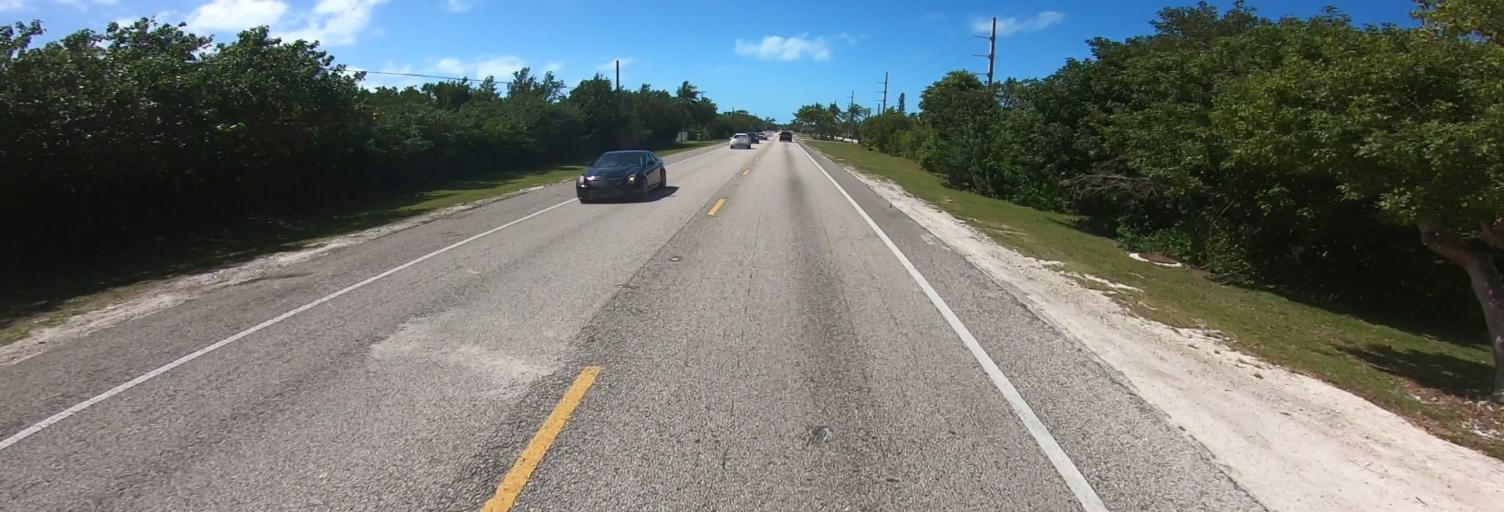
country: US
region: Florida
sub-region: Monroe County
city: Islamorada
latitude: 24.8703
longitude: -80.7051
